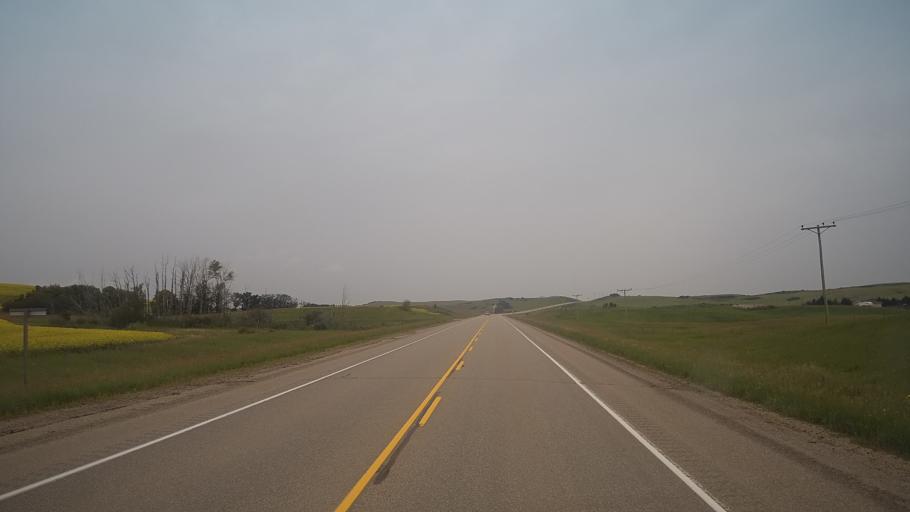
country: CA
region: Saskatchewan
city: Biggar
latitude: 52.0564
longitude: -107.8629
